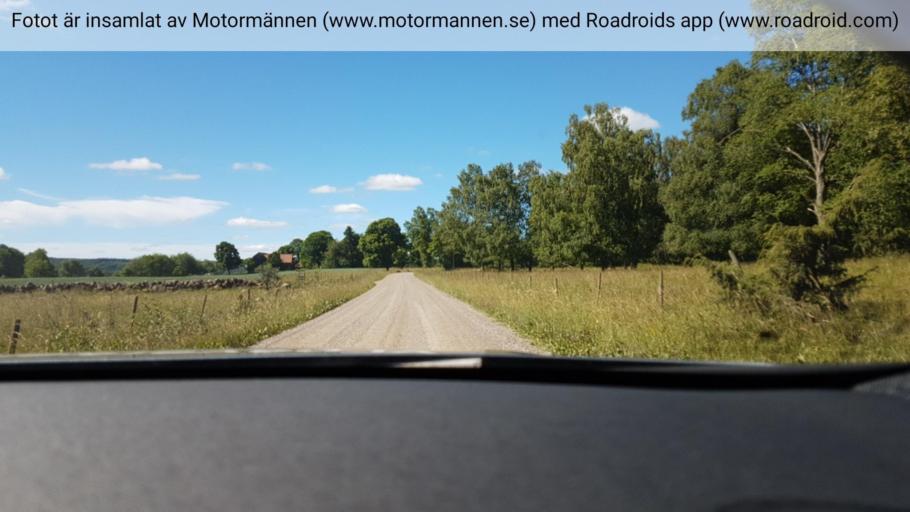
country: SE
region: Vaestra Goetaland
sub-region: Falkopings Kommun
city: Akarp
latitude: 58.2132
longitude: 13.7561
